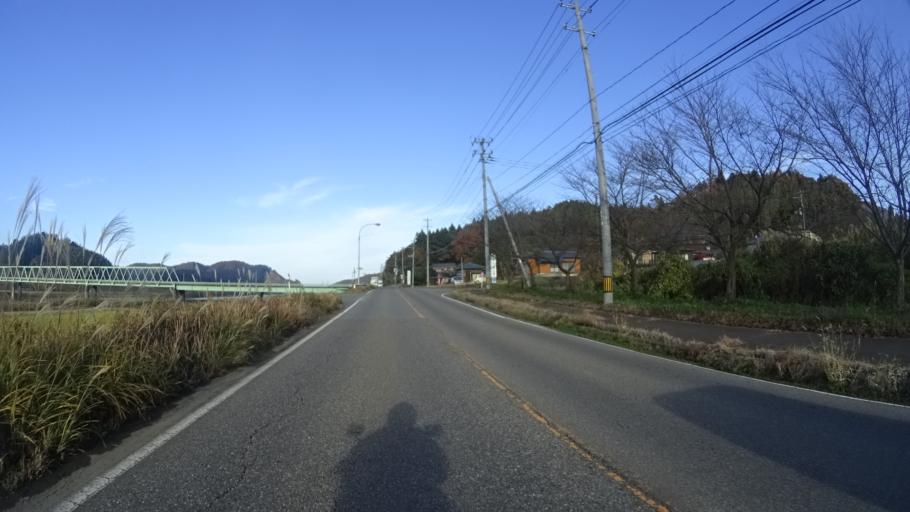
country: JP
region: Niigata
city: Yoshida-kasugacho
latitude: 37.6523
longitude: 138.8102
